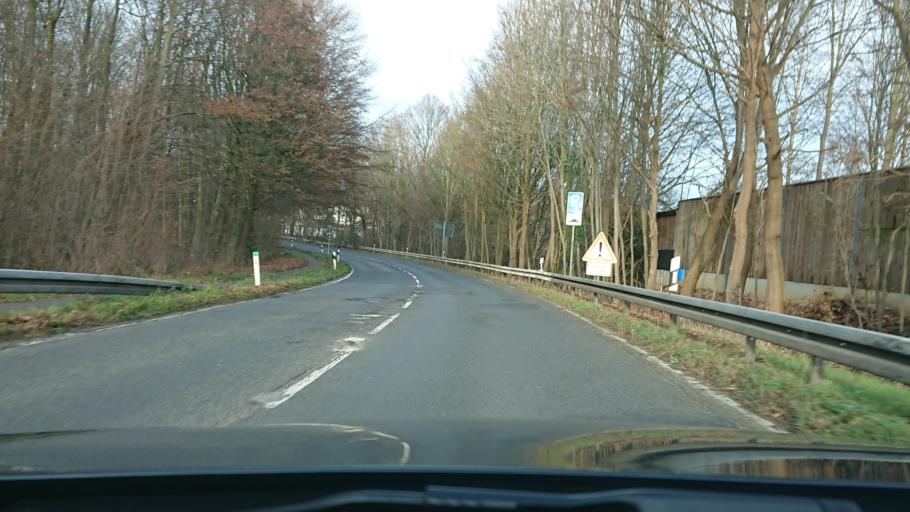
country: DE
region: North Rhine-Westphalia
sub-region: Regierungsbezirk Koln
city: Frechen
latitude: 50.8837
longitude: 6.8222
